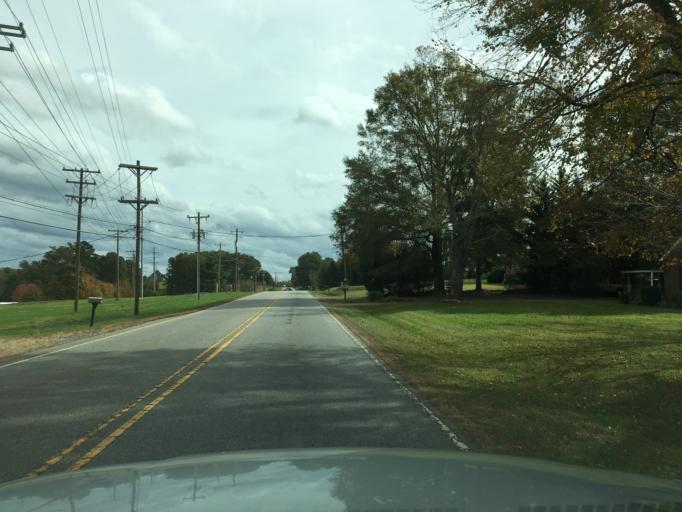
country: US
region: North Carolina
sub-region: Catawba County
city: Hickory
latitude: 35.6953
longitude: -81.2895
